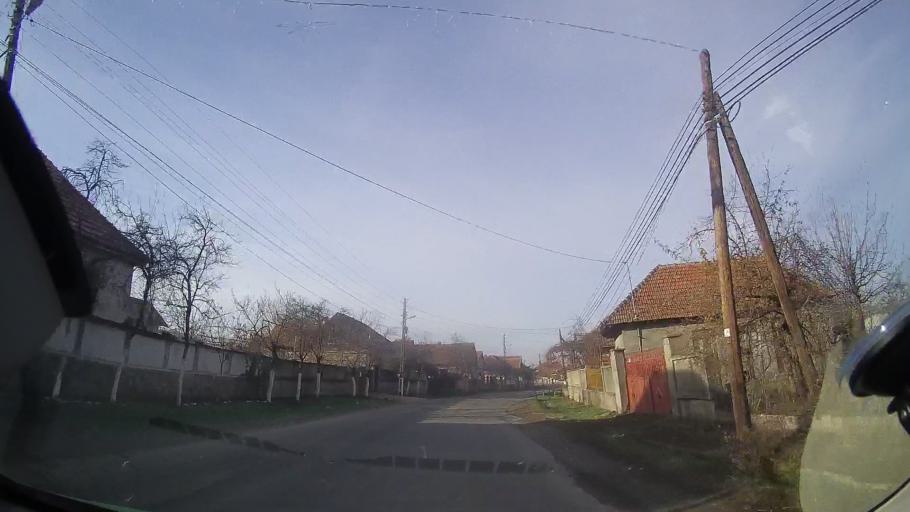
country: RO
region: Bihor
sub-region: Comuna Brusturi
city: Brusturi
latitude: 47.1578
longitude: 22.2377
